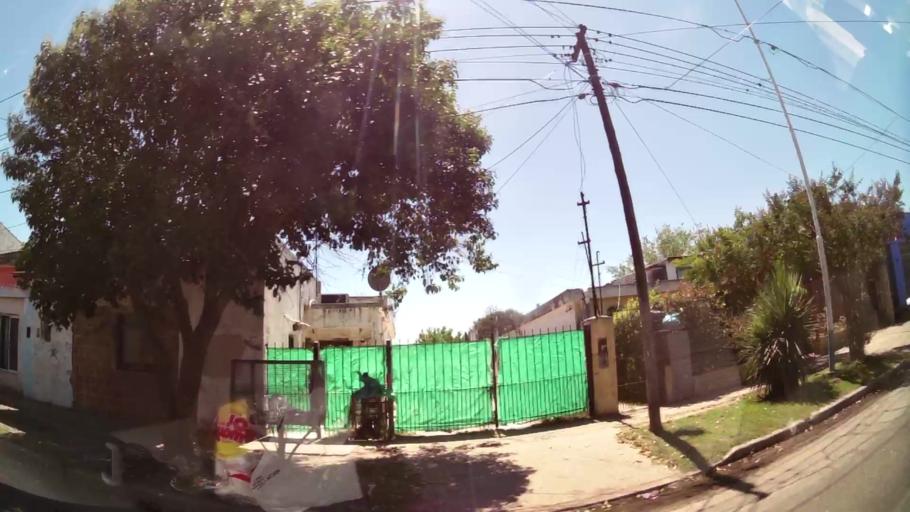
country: AR
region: Buenos Aires
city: Hurlingham
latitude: -34.4932
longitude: -58.6704
